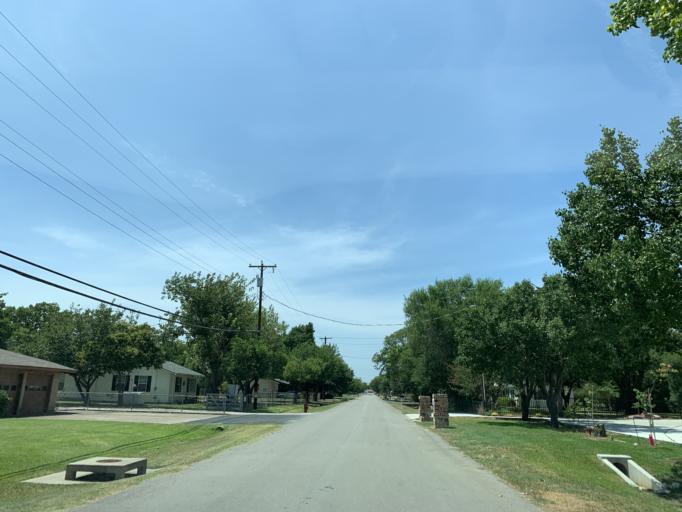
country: US
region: Texas
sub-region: Dallas County
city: Cedar Hill
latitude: 32.6475
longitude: -97.0218
